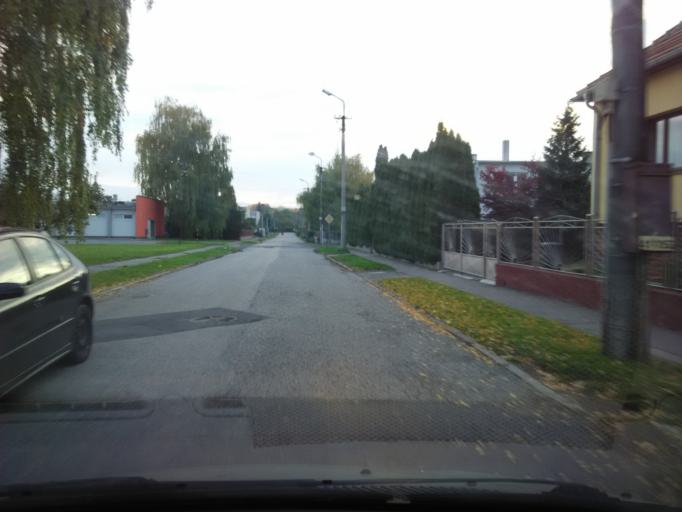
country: SK
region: Nitriansky
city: Levice
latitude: 48.2129
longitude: 18.6181
